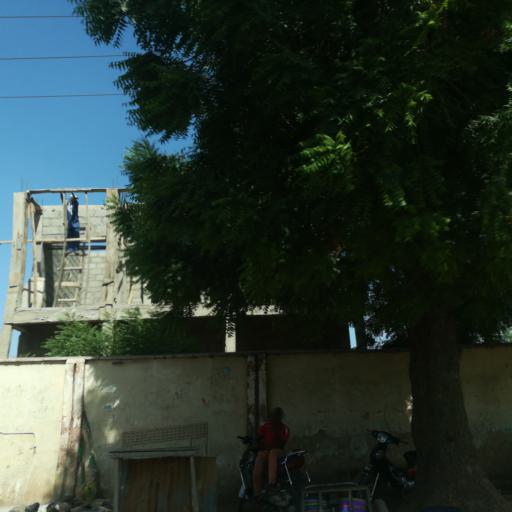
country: NG
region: Kano
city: Kano
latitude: 11.9976
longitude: 8.5295
